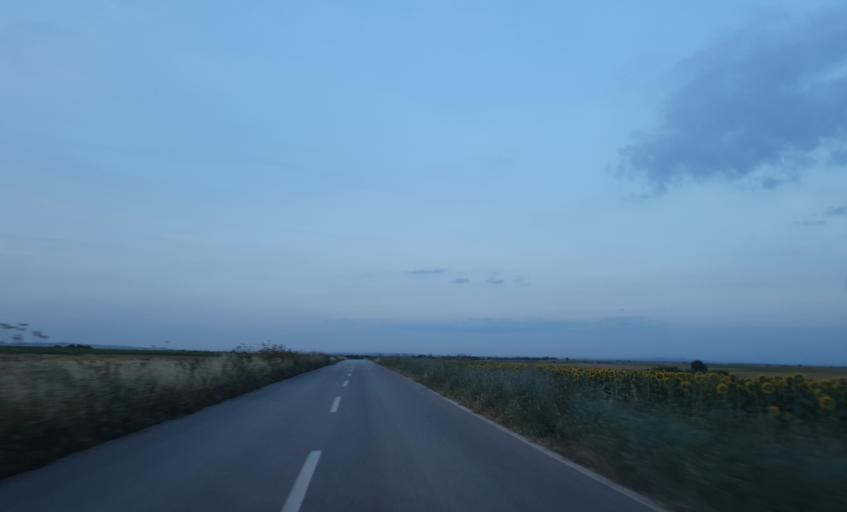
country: TR
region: Tekirdag
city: Beyazkoy
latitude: 41.4264
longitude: 27.6791
